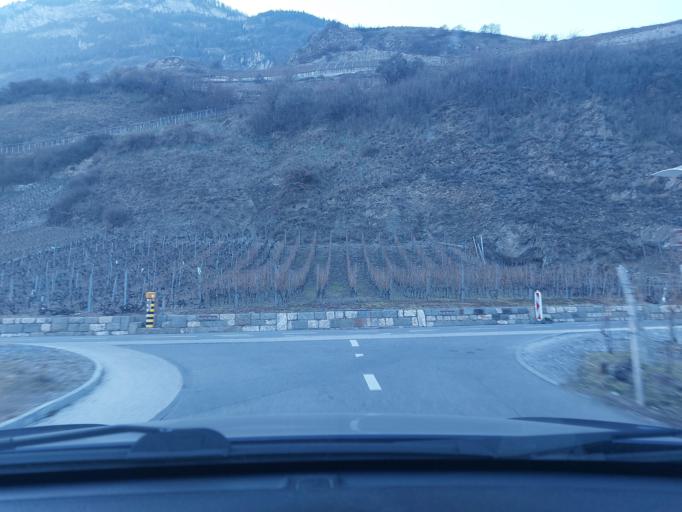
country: CH
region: Valais
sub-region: Martigny District
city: Saillon
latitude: 46.1744
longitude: 7.1883
